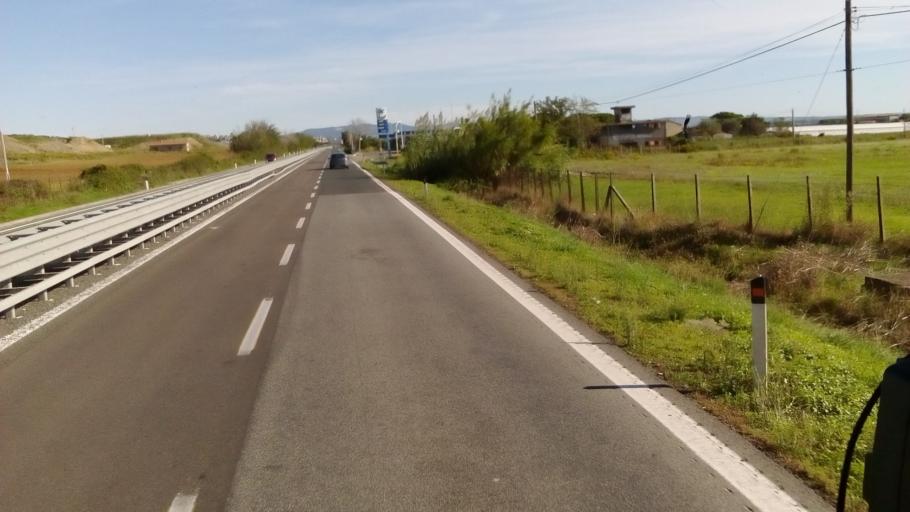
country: IT
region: Latium
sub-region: Provincia di Viterbo
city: Tarquinia
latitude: 42.2746
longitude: 11.7072
